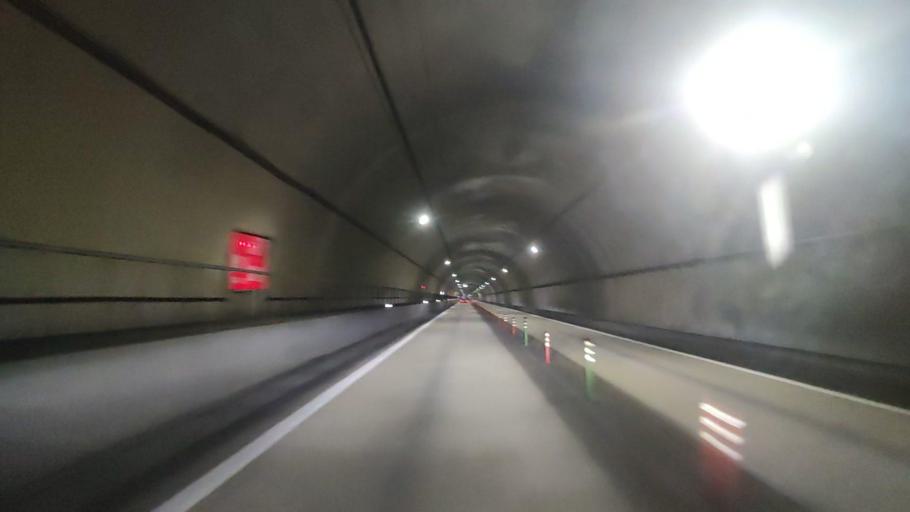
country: JP
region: Wakayama
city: Tanabe
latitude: 33.5439
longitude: 135.5249
